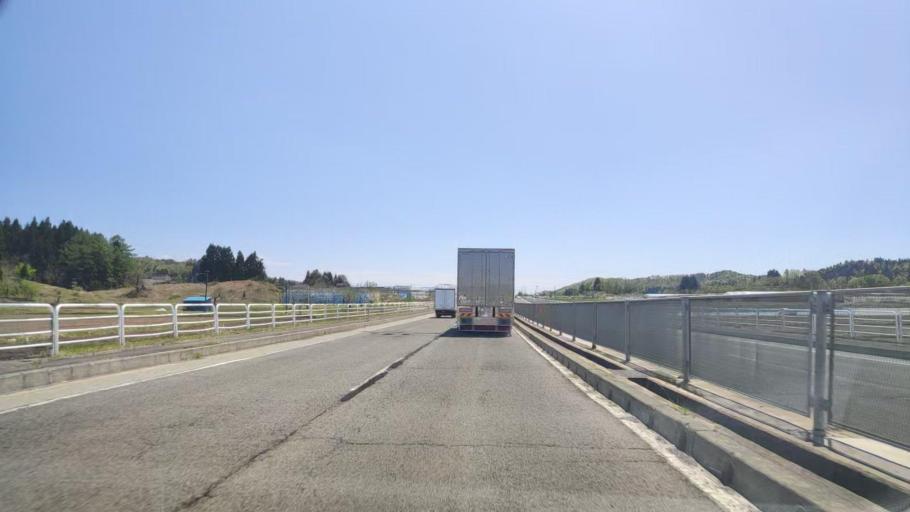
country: JP
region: Yamagata
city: Obanazawa
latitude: 38.5431
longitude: 140.3958
